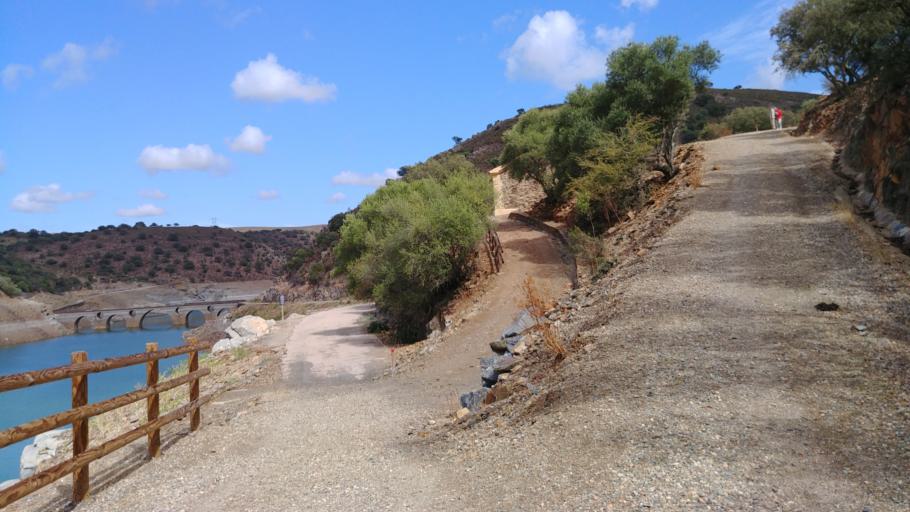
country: ES
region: Extremadura
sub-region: Provincia de Caceres
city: Torrejon el Rubio
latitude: 39.8313
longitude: -6.0289
